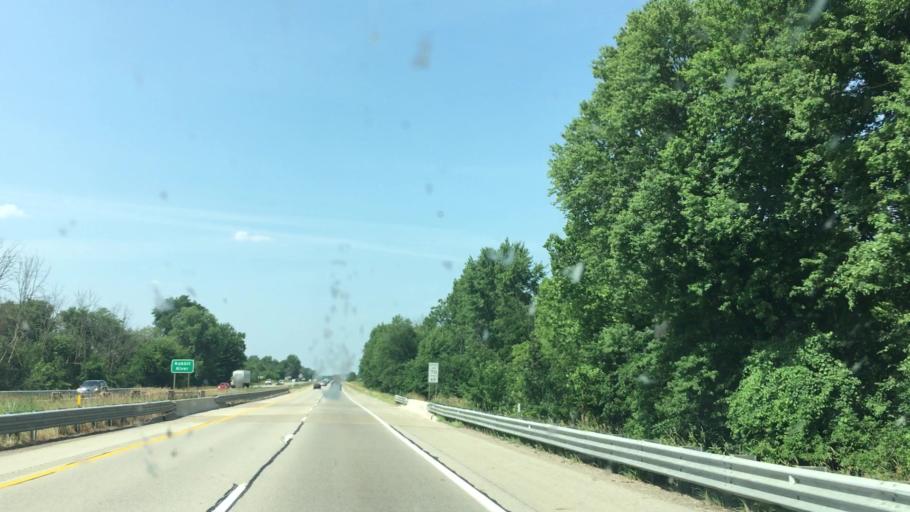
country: US
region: Michigan
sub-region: Allegan County
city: Wayland
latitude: 42.6833
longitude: -85.6606
